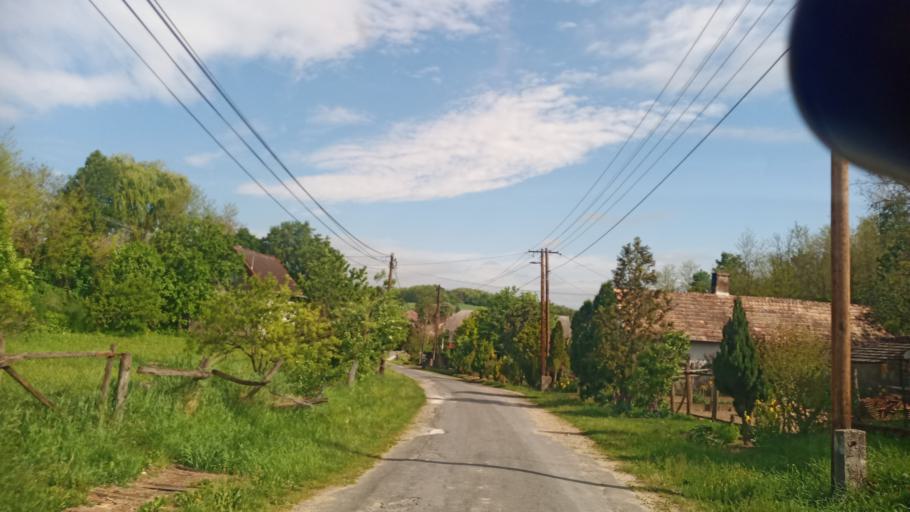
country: HU
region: Zala
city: Pacsa
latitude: 46.6697
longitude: 17.0792
